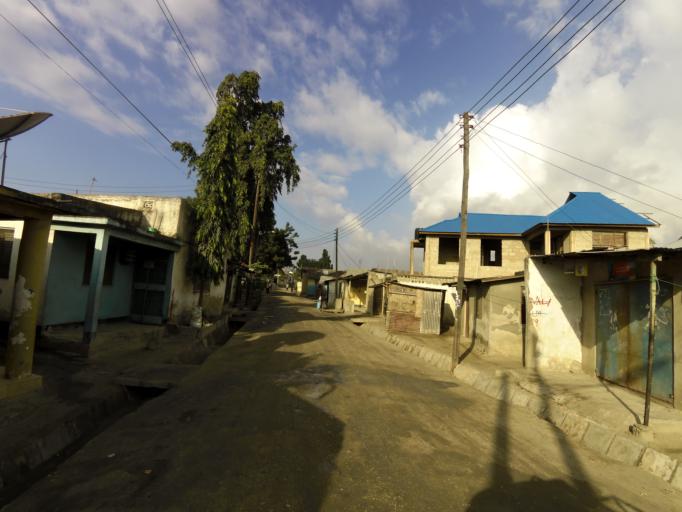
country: TZ
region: Dar es Salaam
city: Magomeni
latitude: -6.7917
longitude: 39.2288
